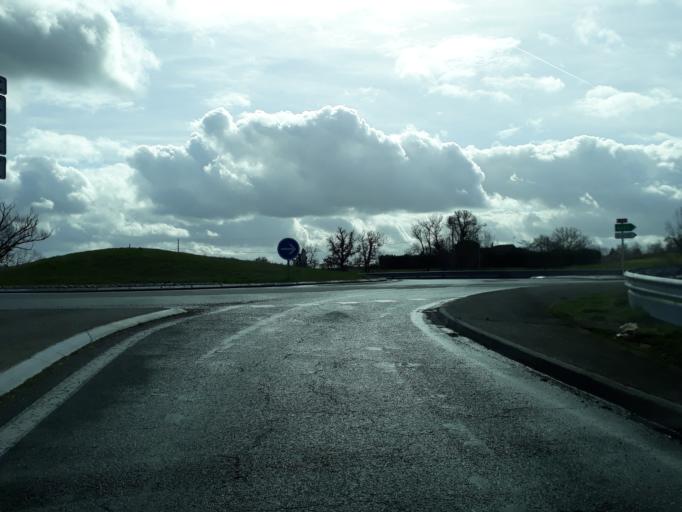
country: FR
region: Midi-Pyrenees
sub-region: Departement du Gers
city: Pujaudran
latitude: 43.6034
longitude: 1.0464
